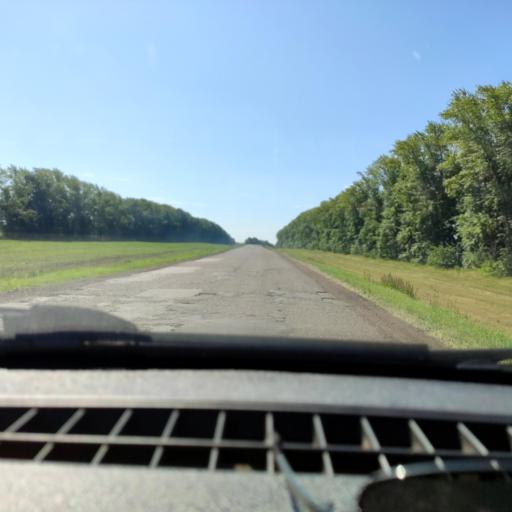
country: RU
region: Bashkortostan
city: Karmaskaly
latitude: 54.3923
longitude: 56.1724
